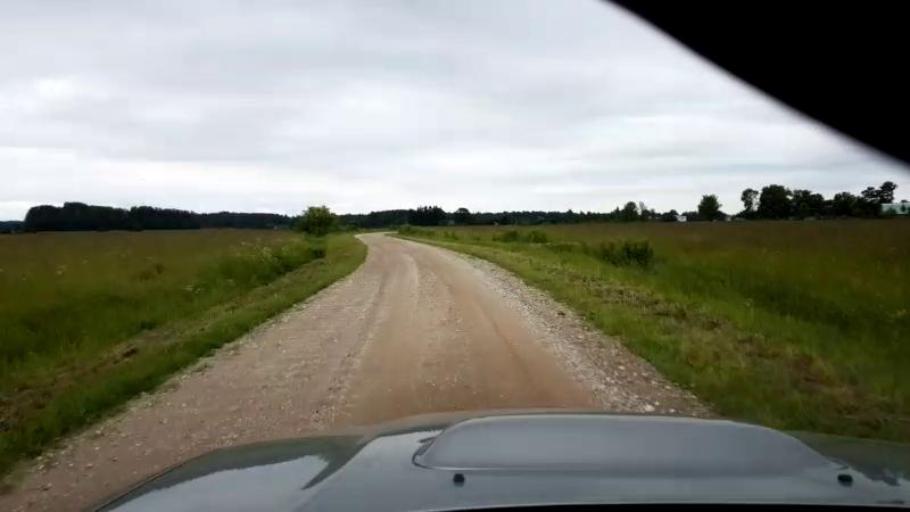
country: EE
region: Paernumaa
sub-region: Halinga vald
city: Parnu-Jaagupi
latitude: 58.5353
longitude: 24.5606
